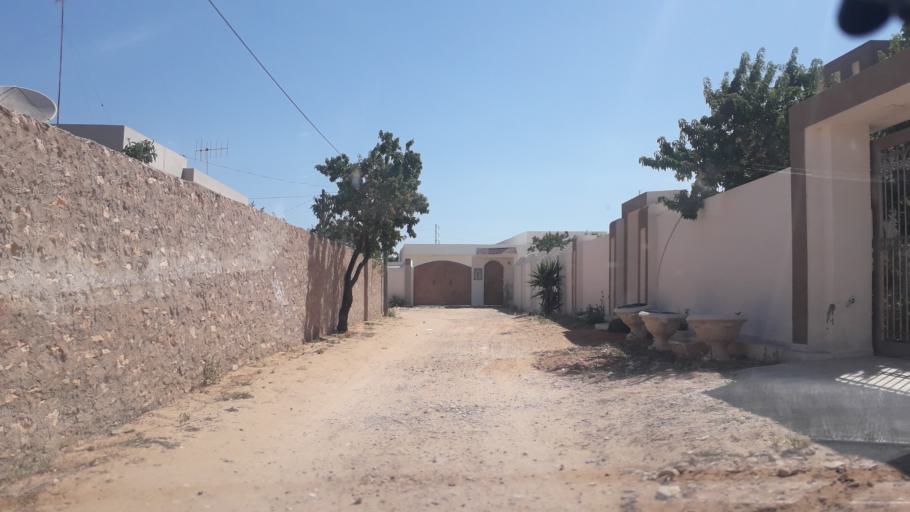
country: TN
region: Safaqis
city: Al Qarmadah
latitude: 34.8332
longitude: 10.7674
